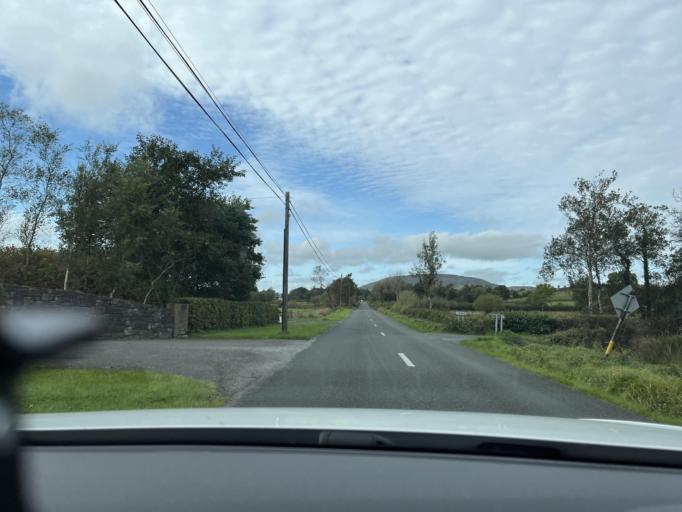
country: IE
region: Connaught
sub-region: Roscommon
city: Boyle
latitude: 54.0242
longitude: -8.4027
